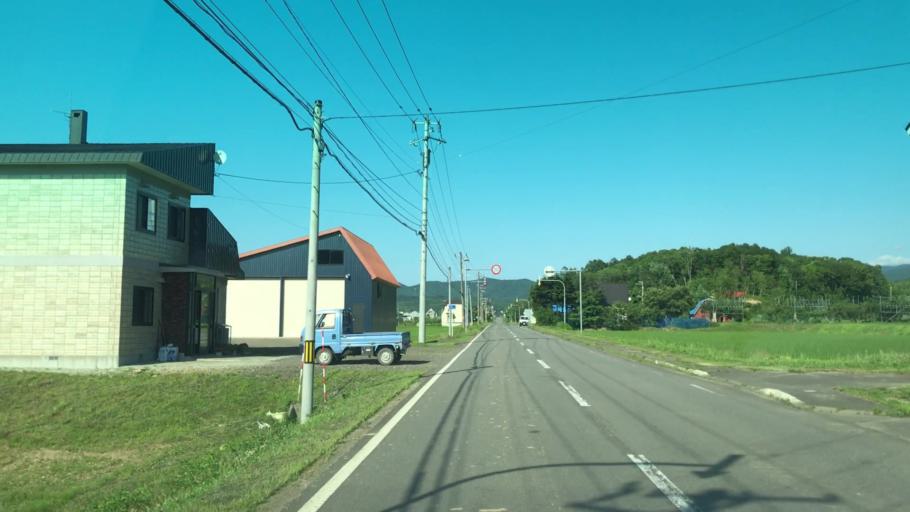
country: JP
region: Hokkaido
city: Yoichi
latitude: 43.0380
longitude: 140.7872
